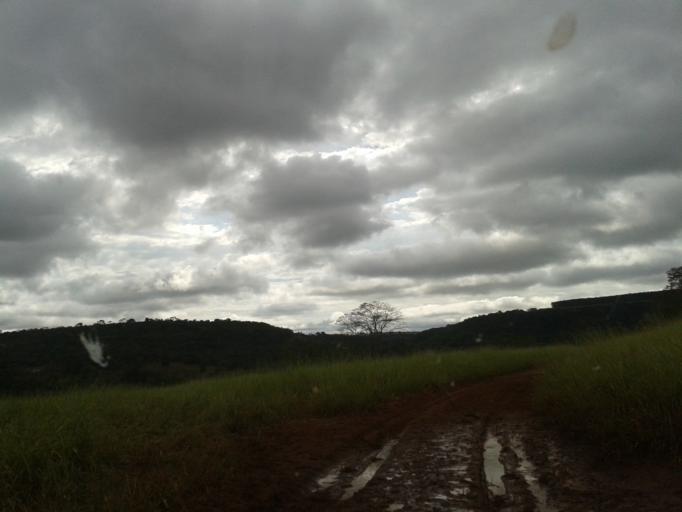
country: BR
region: Minas Gerais
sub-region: Campina Verde
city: Campina Verde
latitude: -19.4676
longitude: -49.5926
